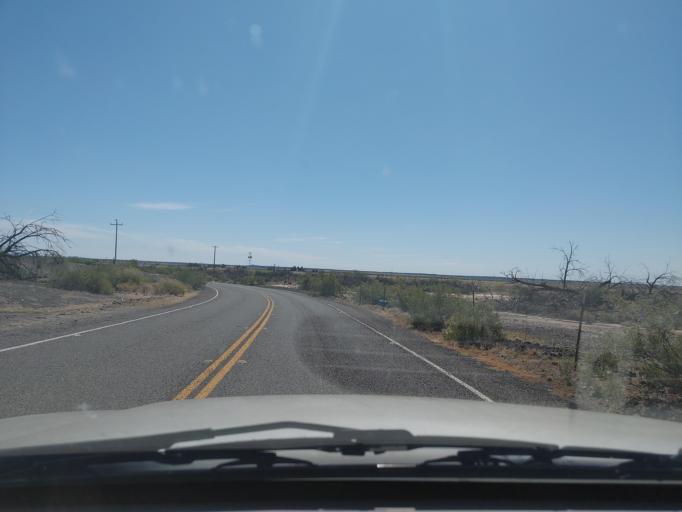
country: US
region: Arizona
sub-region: Maricopa County
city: Gila Bend
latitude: 32.9838
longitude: -113.3259
